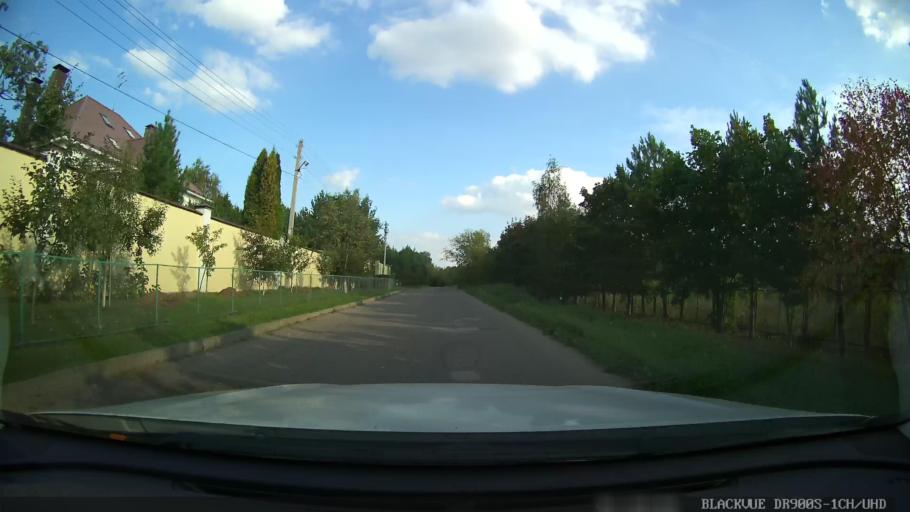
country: RU
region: Moskovskaya
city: Nemchinovka
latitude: 55.7398
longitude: 37.3403
